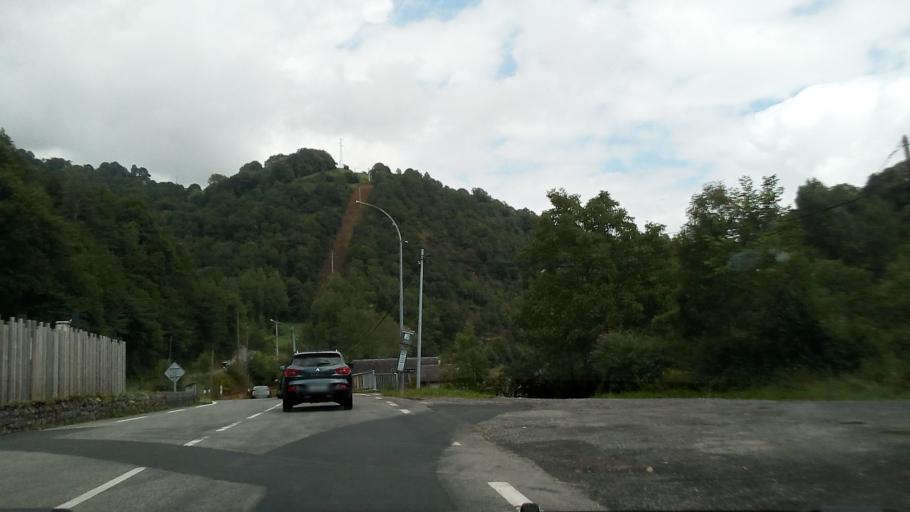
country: FR
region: Aquitaine
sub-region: Departement des Pyrenees-Atlantiques
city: Arette
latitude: 43.0340
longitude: -0.6058
